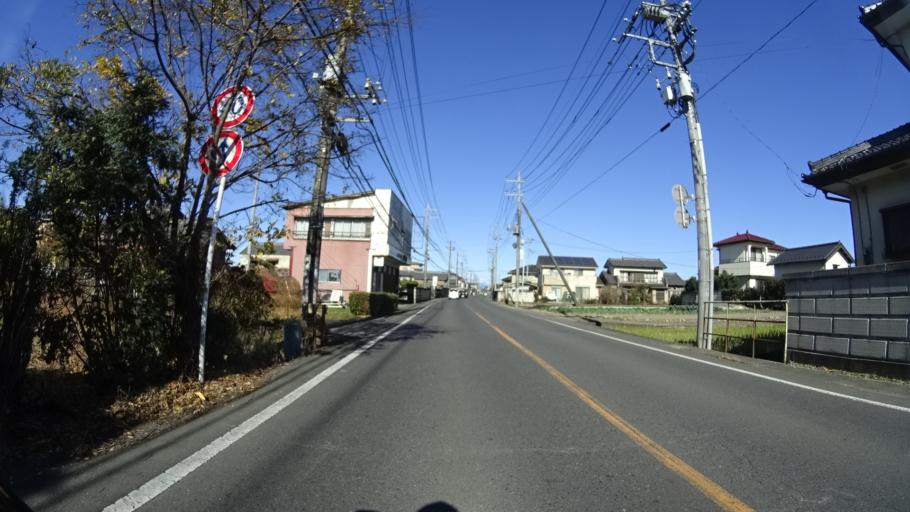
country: JP
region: Tochigi
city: Mibu
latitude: 36.4389
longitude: 139.7516
